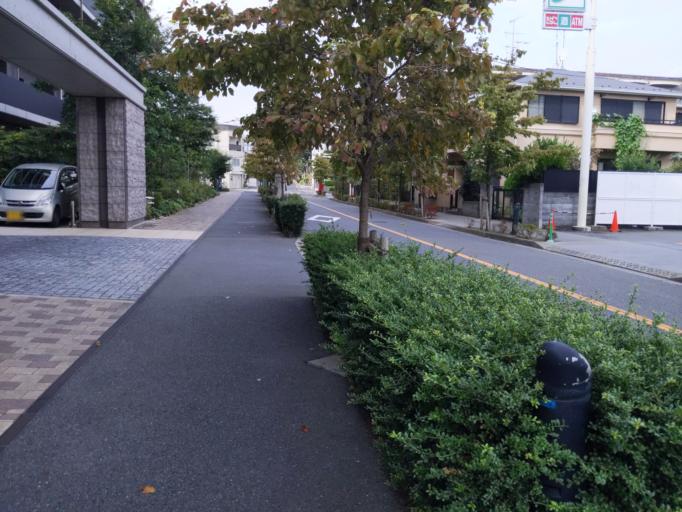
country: JP
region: Tokyo
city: Tokyo
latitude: 35.6521
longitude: 139.6286
